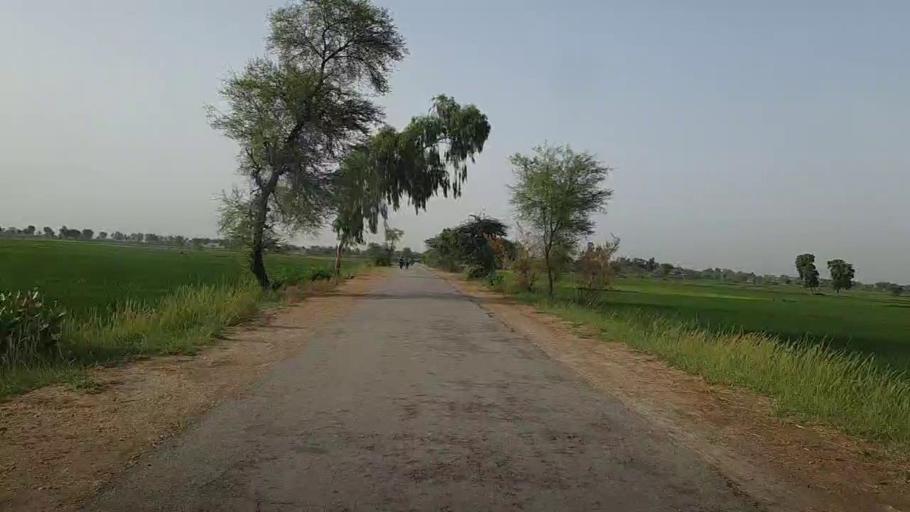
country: PK
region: Sindh
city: Khairpur Nathan Shah
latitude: 27.1241
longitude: 67.7894
